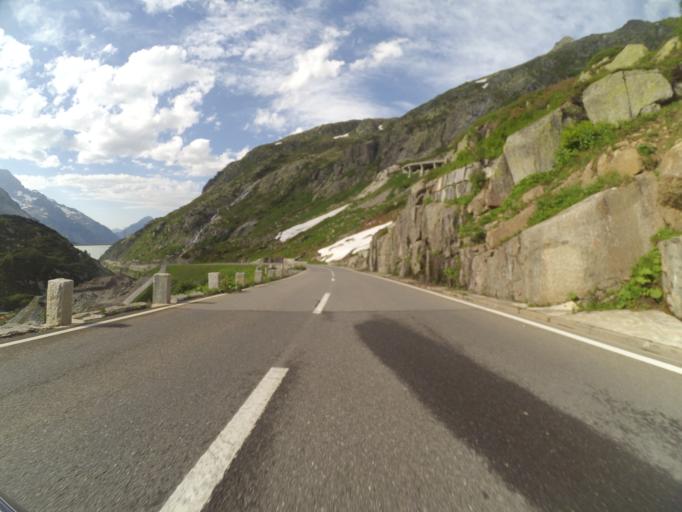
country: CH
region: Bern
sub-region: Interlaken-Oberhasli District
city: Meiringen
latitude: 46.5746
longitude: 8.3378
